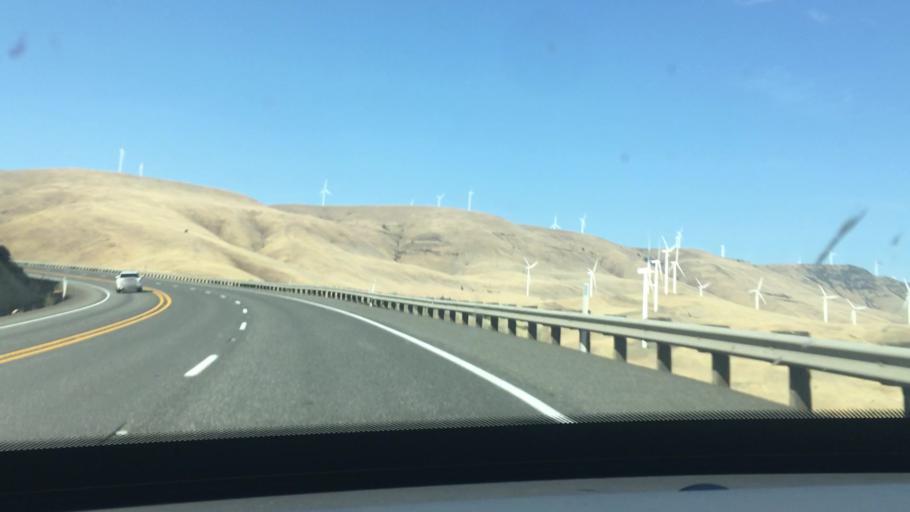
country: US
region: Washington
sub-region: Klickitat County
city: Goldendale
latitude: 45.7103
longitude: -120.8013
